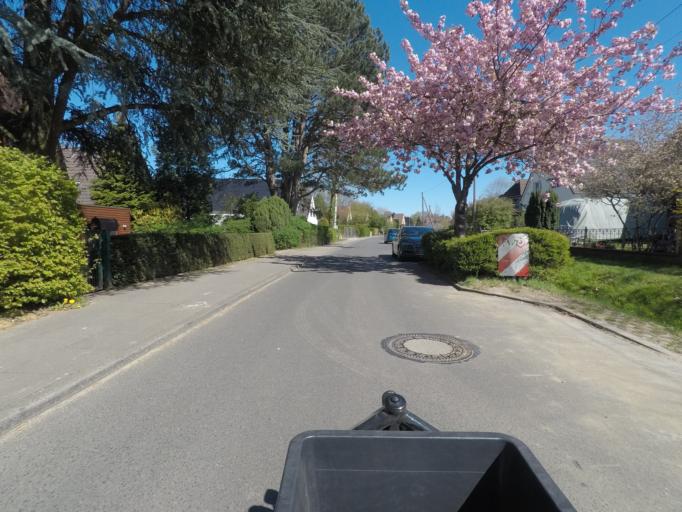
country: DE
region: Hamburg
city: Farmsen-Berne
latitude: 53.5935
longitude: 10.1274
